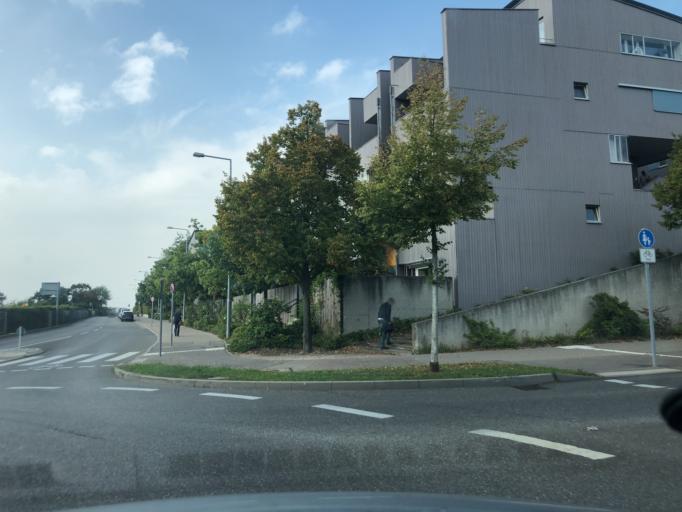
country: DE
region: Baden-Wuerttemberg
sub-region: Regierungsbezirk Stuttgart
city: Stuttgart Feuerbach
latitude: 48.8159
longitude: 9.1883
